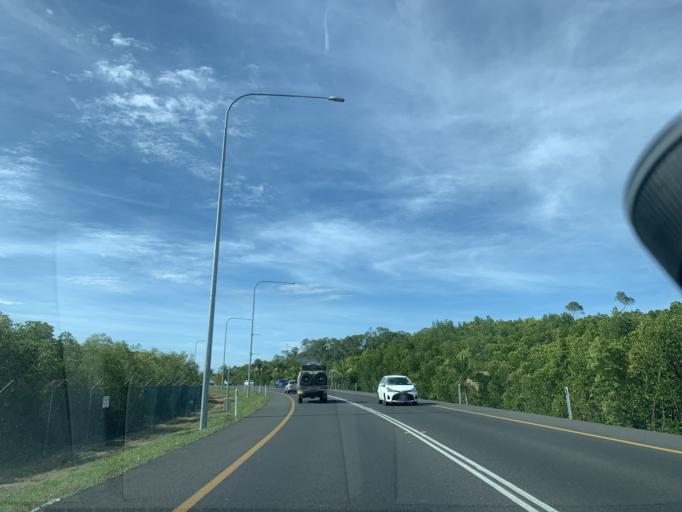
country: AU
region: Queensland
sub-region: Cairns
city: Cairns
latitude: -16.8871
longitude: 145.7624
